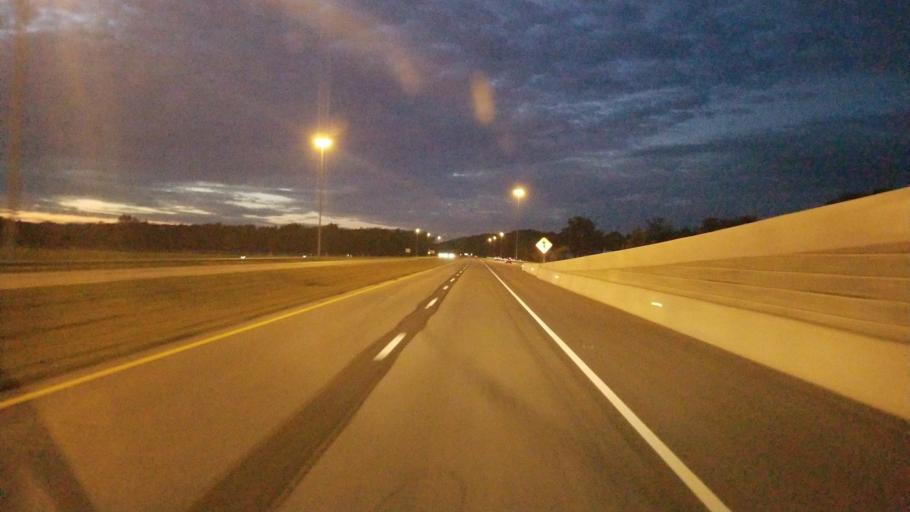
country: US
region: Ohio
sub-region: Scioto County
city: Lucasville
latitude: 38.8944
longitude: -83.0010
